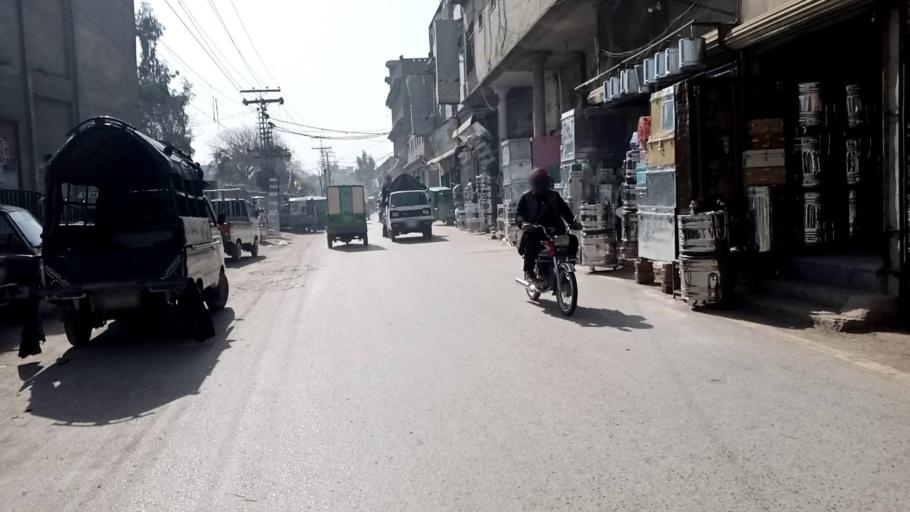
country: PK
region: Khyber Pakhtunkhwa
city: Peshawar
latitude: 34.0047
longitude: 71.5848
